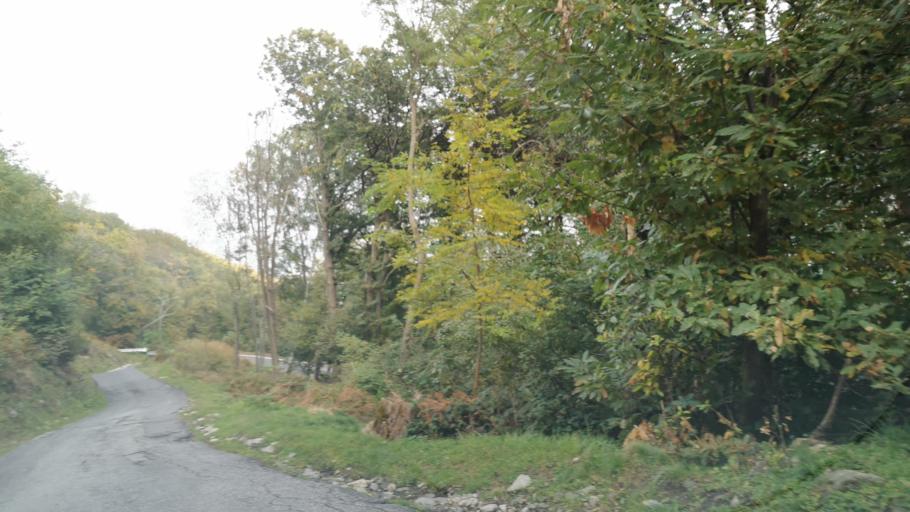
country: IT
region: Lombardy
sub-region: Provincia di Como
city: San Siro
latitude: 46.0700
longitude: 9.2546
